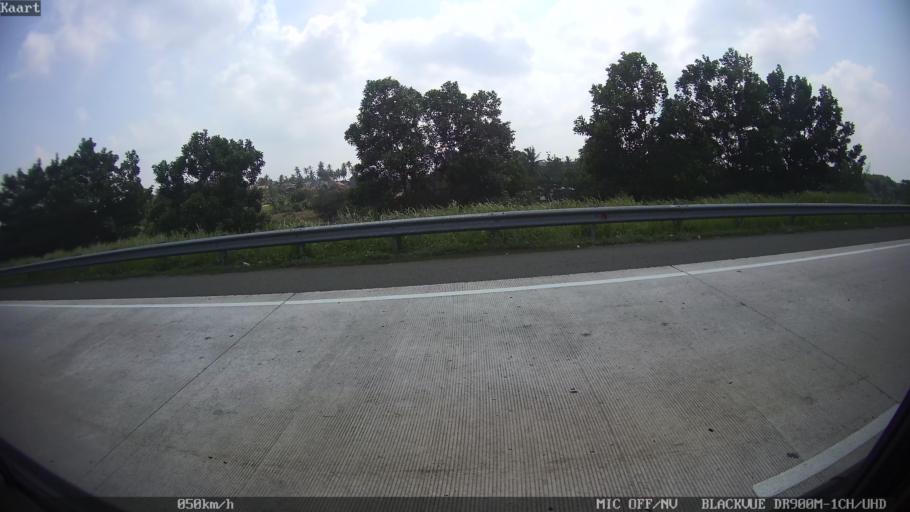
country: ID
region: Lampung
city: Kedaton
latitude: -5.3510
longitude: 105.3221
